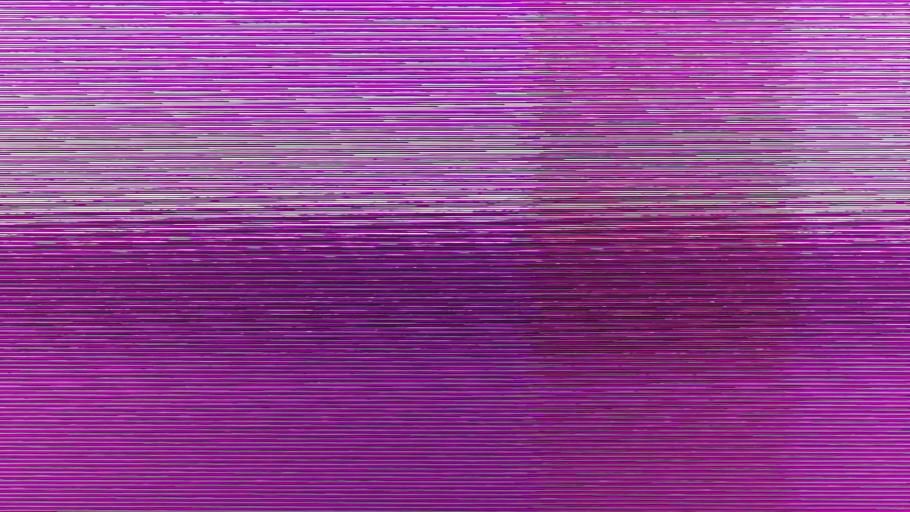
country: US
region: Michigan
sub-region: Genesee County
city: Linden
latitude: 42.8165
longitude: -83.7824
